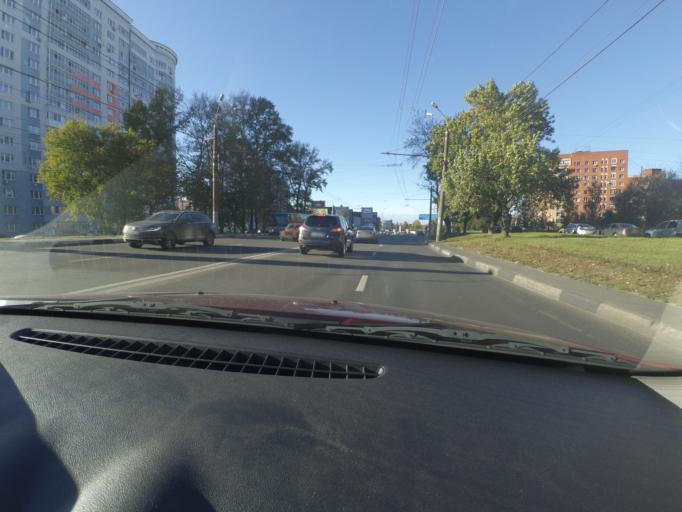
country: RU
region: Nizjnij Novgorod
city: Bor
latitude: 56.3130
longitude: 44.0721
